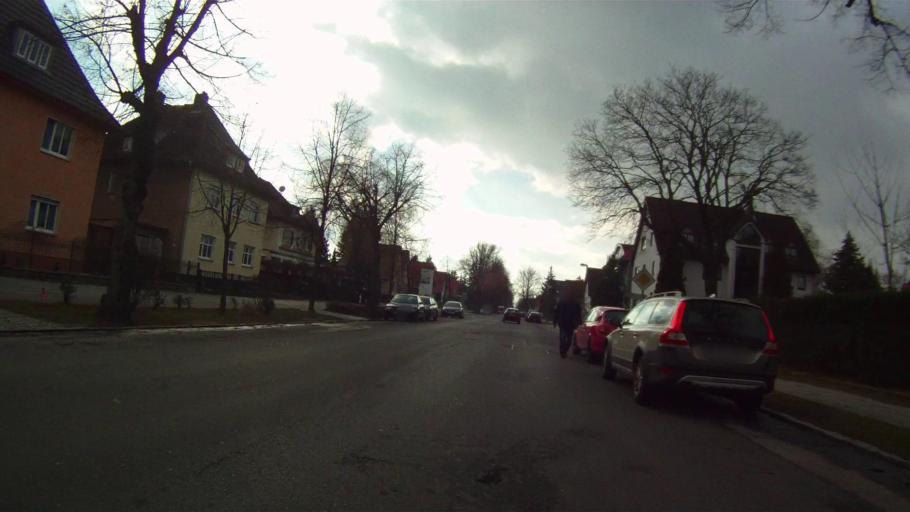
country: DE
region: Berlin
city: Biesdorf
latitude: 52.5233
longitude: 13.5566
